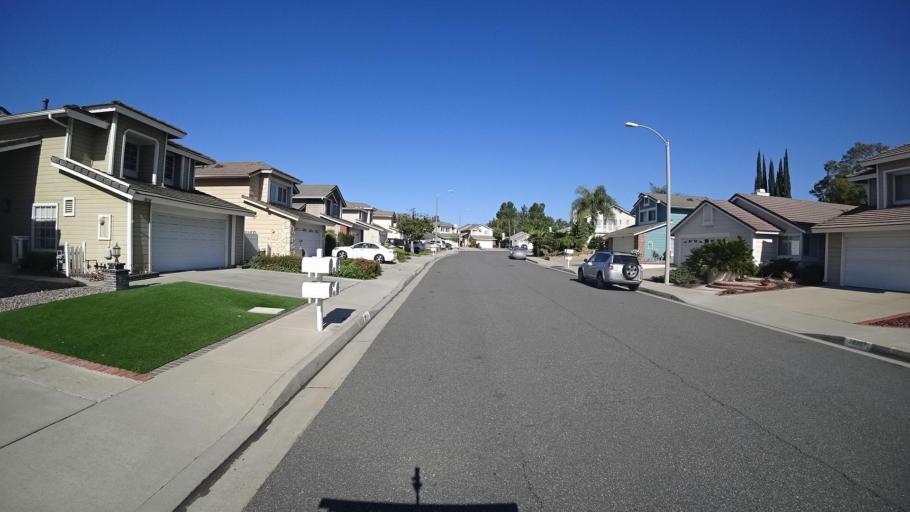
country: US
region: California
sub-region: Los Angeles County
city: Walnut
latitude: 33.9759
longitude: -117.8536
